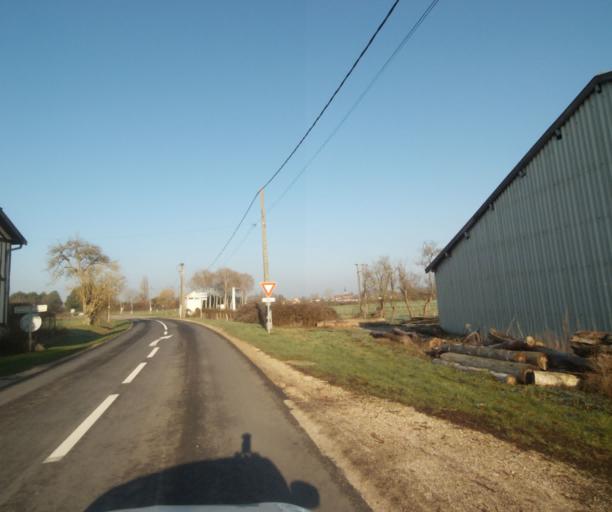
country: FR
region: Champagne-Ardenne
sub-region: Departement de la Haute-Marne
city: Montier-en-Der
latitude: 48.4640
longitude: 4.7653
